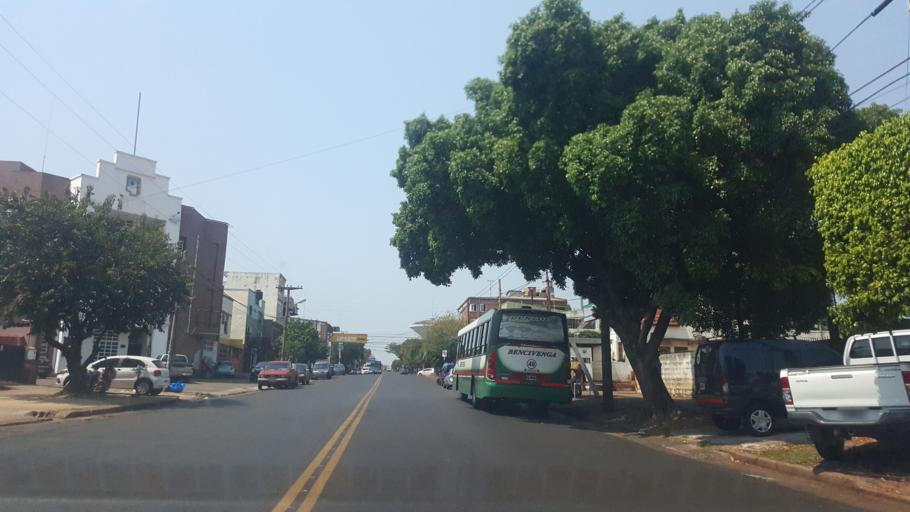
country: AR
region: Misiones
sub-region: Departamento de Capital
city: Posadas
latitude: -27.3733
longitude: -55.9073
